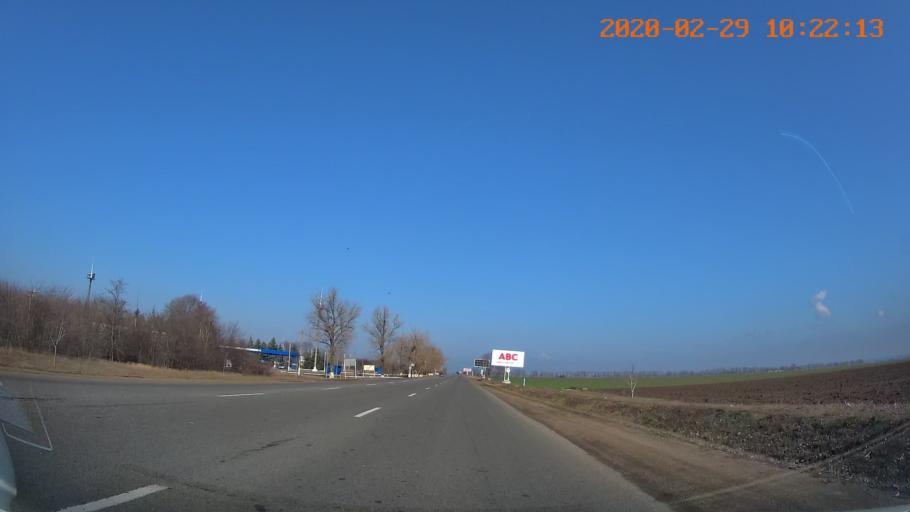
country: MD
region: Telenesti
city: Tiraspolul Nou
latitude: 46.8736
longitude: 29.6076
